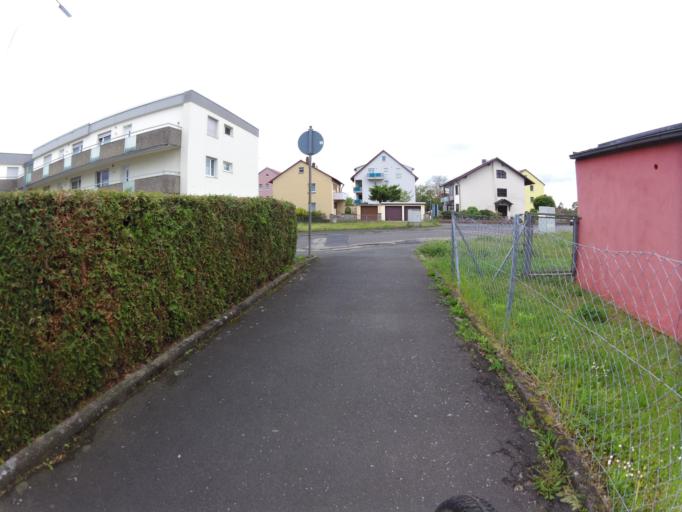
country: DE
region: Bavaria
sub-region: Regierungsbezirk Unterfranken
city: Volkach
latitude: 49.8599
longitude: 10.2376
